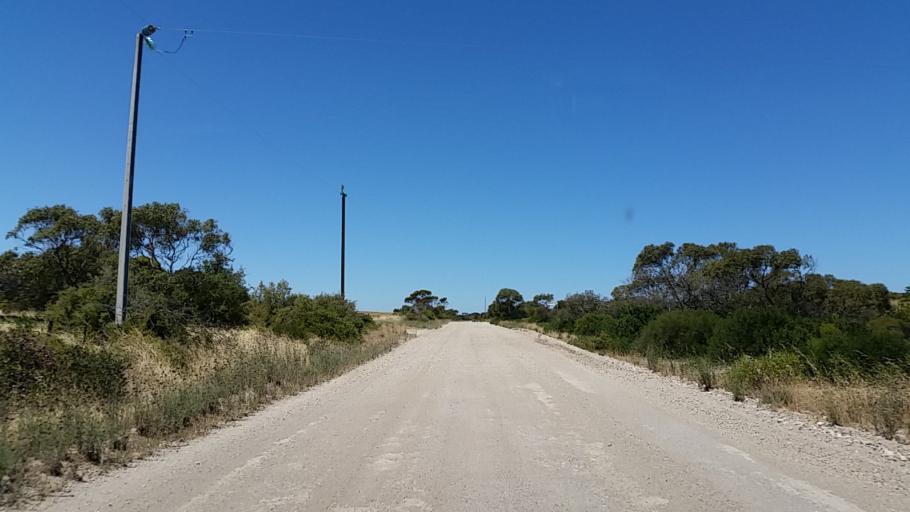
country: AU
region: South Australia
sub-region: Yorke Peninsula
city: Honiton
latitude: -35.1190
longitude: 137.3570
